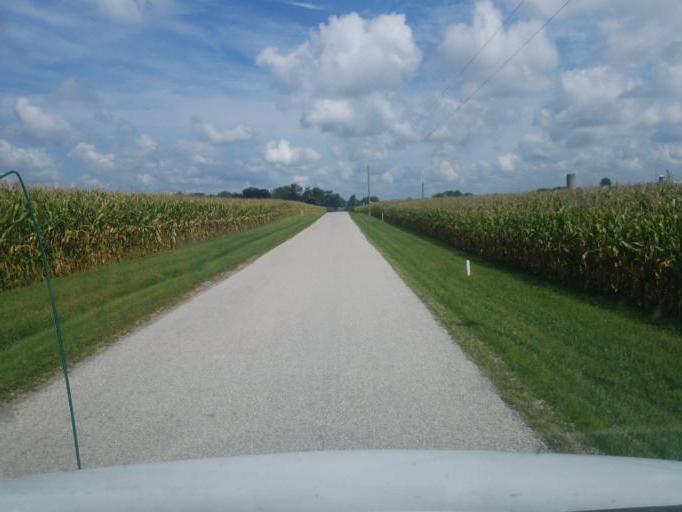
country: US
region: Ohio
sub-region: Marion County
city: Marion
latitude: 40.5053
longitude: -83.0837
